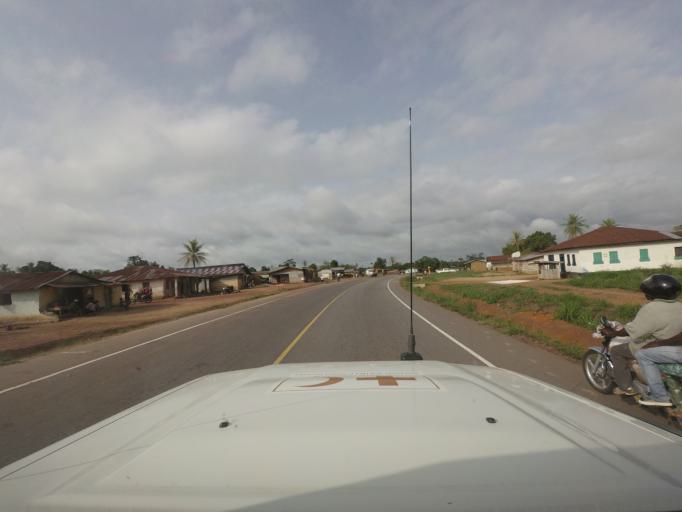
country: LR
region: Bong
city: Gbarnga
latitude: 7.0025
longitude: -9.2874
